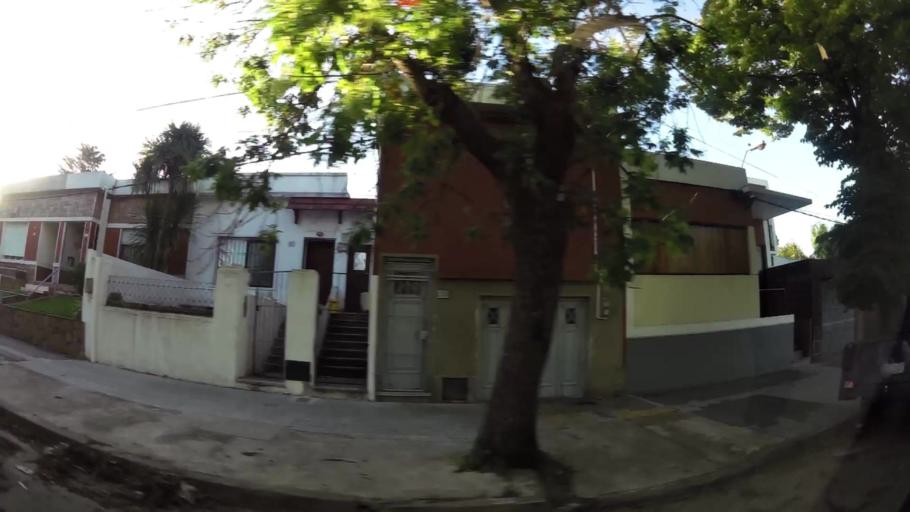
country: UY
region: Montevideo
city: Montevideo
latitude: -34.8414
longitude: -56.2041
